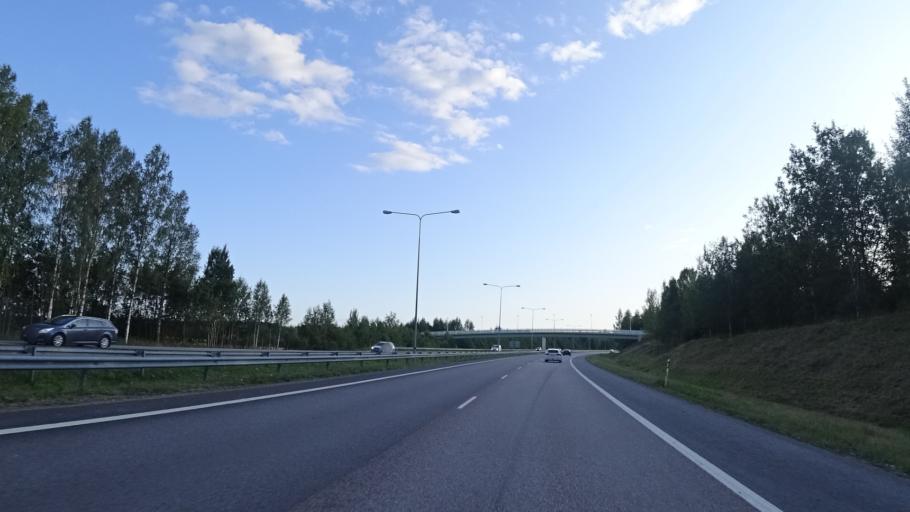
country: FI
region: South Karelia
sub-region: Imatra
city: Ruokolahti
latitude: 61.2090
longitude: 28.8451
